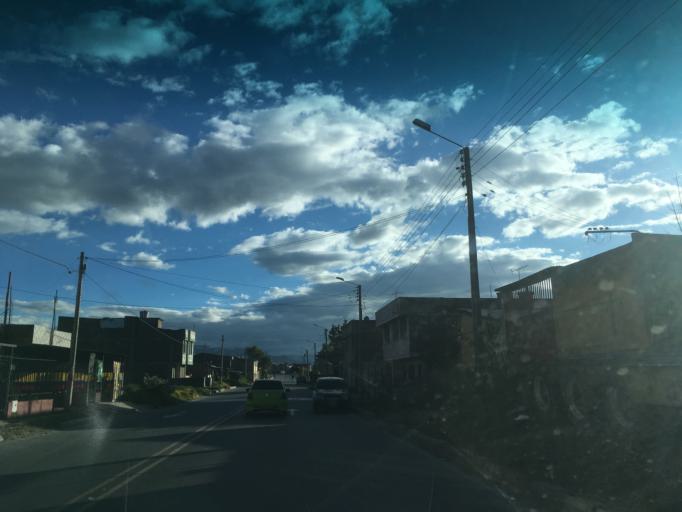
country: CO
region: Boyaca
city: Sogamoso
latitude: 5.7216
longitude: -72.9439
